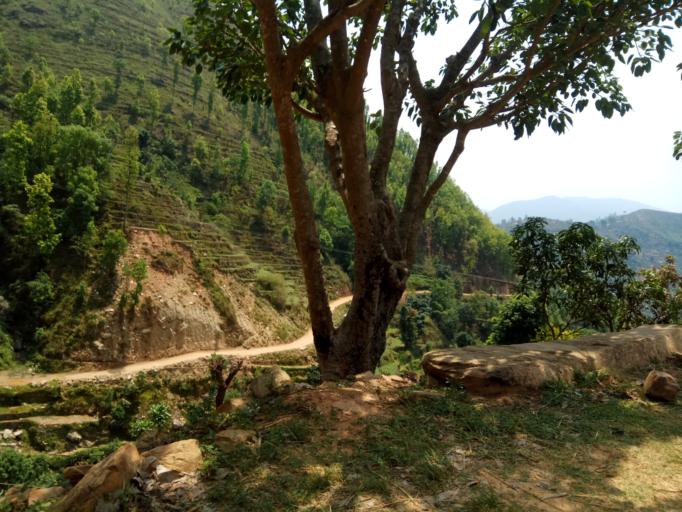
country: NP
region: Central Region
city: Kirtipur
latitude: 27.8967
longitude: 85.0865
